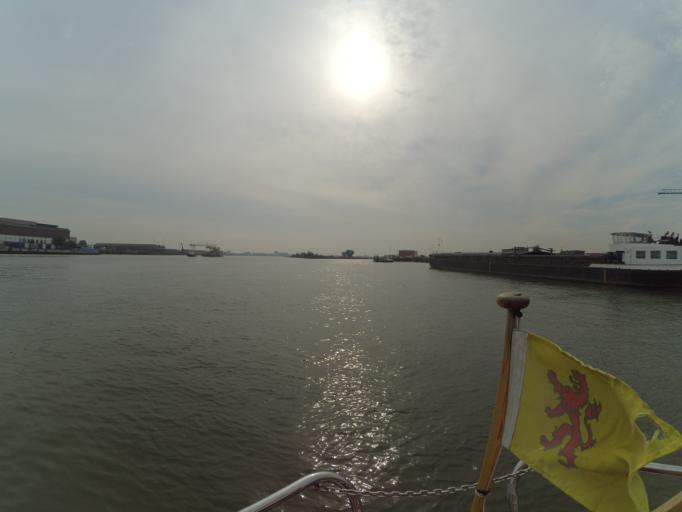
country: NL
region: South Holland
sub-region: Gemeente Alblasserdam
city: Alblasserdam
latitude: 51.8519
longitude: 4.6568
